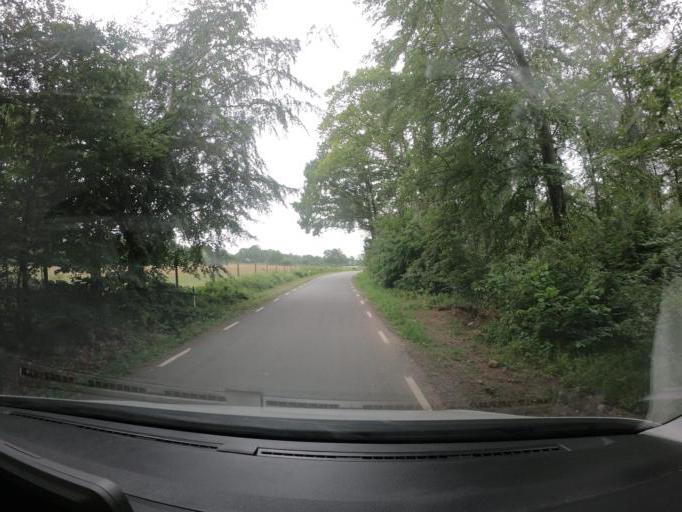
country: SE
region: Skane
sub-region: Hassleholms Kommun
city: Sosdala
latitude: 56.1187
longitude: 13.6434
